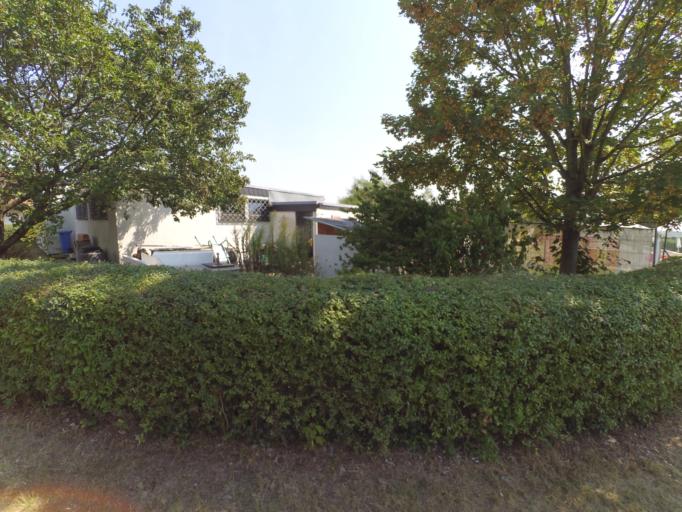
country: DE
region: Baden-Wuerttemberg
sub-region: Karlsruhe Region
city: Ladenburg
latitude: 49.4652
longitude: 8.6123
